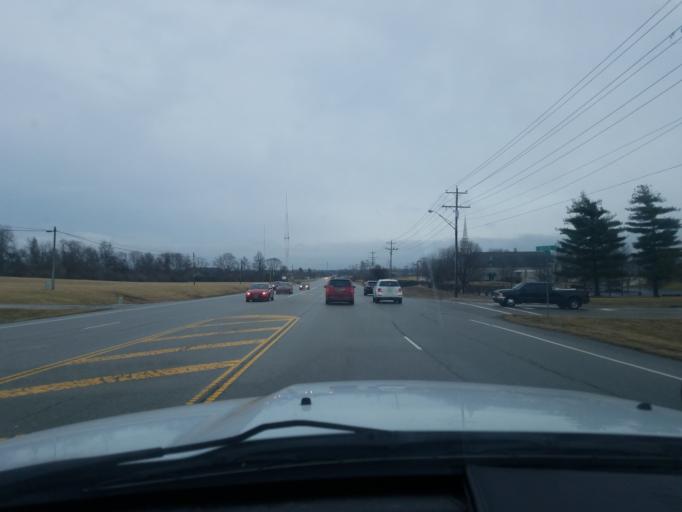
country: US
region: Ohio
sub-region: Warren County
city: Mason
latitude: 39.3518
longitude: -84.3409
